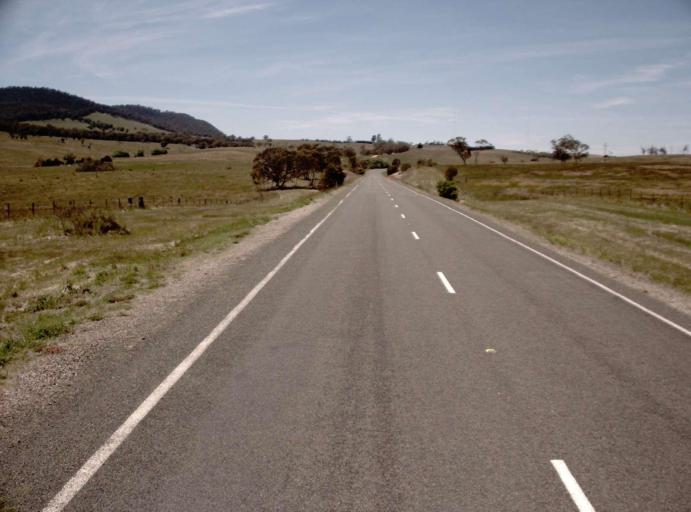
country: AU
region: Victoria
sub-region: Alpine
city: Mount Beauty
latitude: -37.1277
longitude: 147.6396
